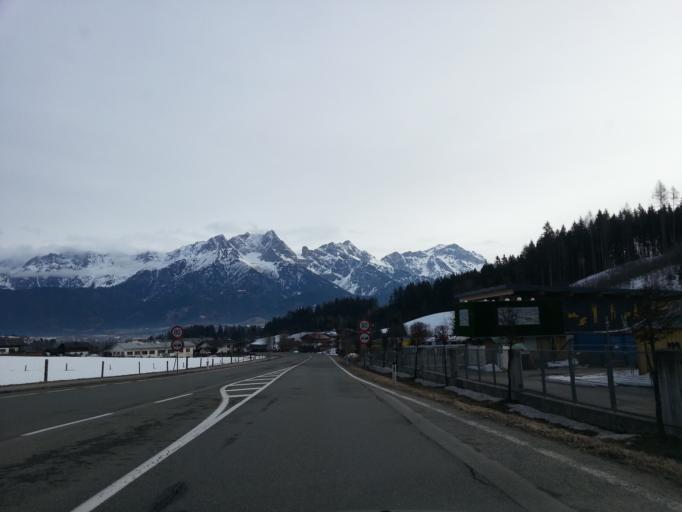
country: AT
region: Salzburg
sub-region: Politischer Bezirk Zell am See
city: Maishofen
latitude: 47.4003
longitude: 12.8048
